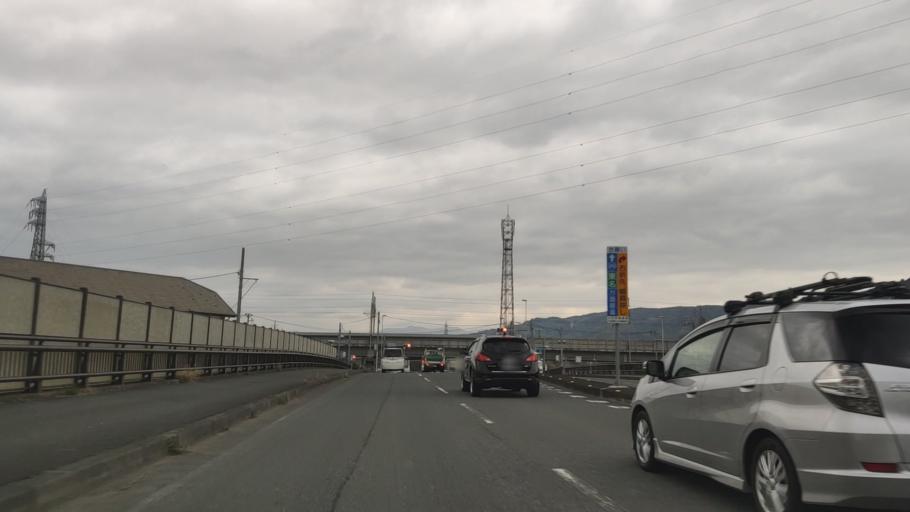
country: JP
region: Kanagawa
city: Odawara
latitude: 35.2868
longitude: 139.1999
